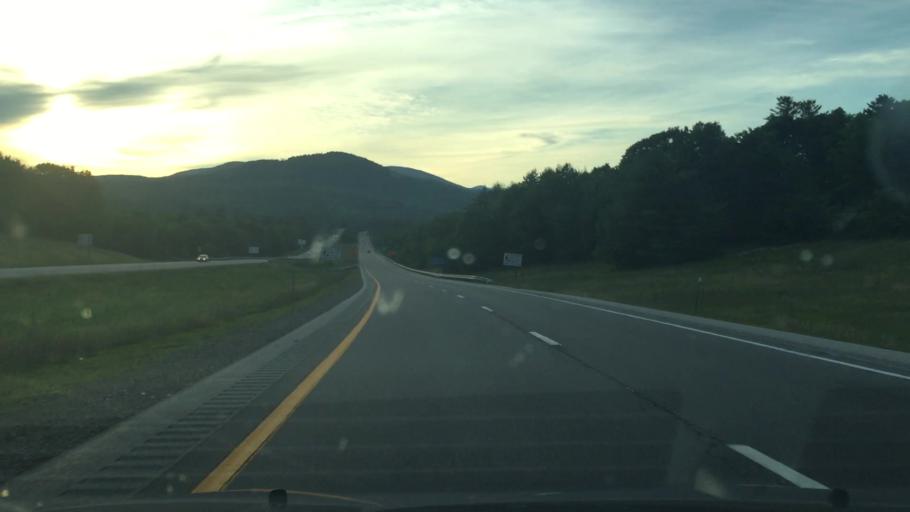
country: US
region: New Hampshire
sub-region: Grafton County
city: Thornton
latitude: 43.8618
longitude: -71.6545
